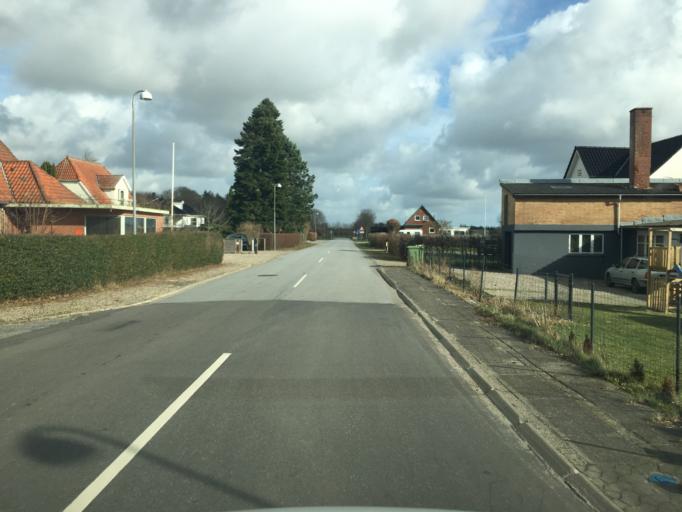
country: DK
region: South Denmark
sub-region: Aabenraa Kommune
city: Krusa
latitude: 54.8972
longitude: 9.4440
